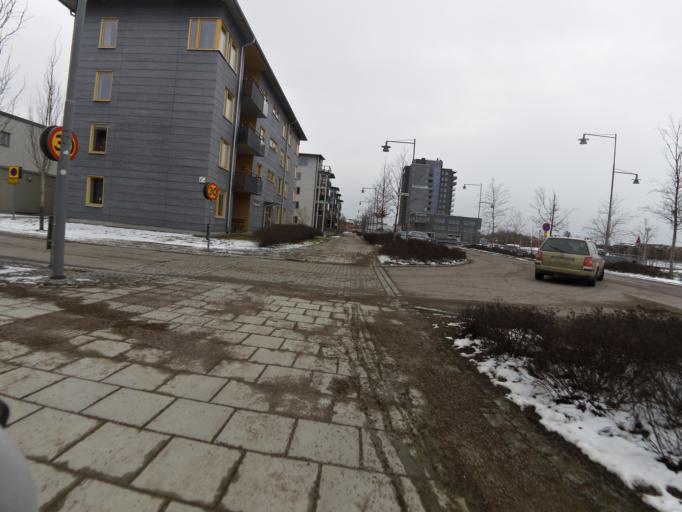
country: SE
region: Gaevleborg
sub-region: Gavle Kommun
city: Gavle
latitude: 60.6803
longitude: 17.1627
